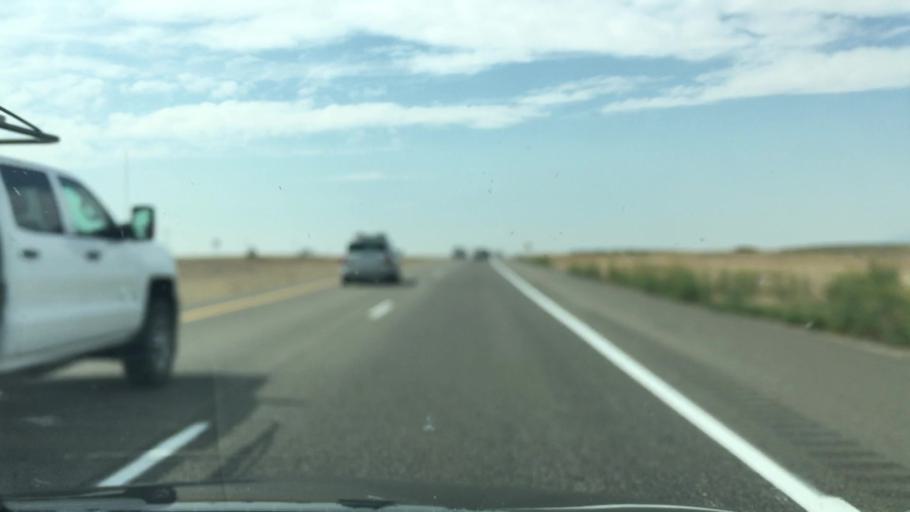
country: US
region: Idaho
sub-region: Ada County
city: Boise
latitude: 43.4650
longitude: -116.0935
